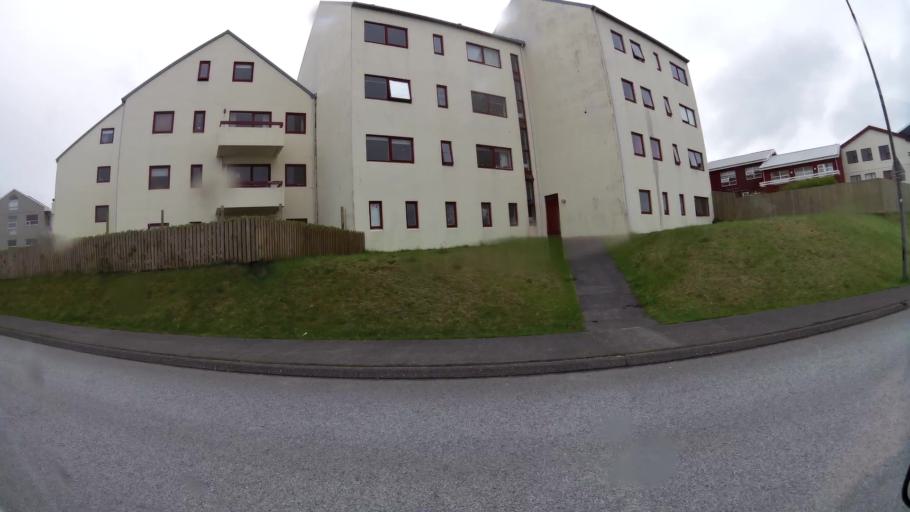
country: IS
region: Capital Region
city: Hafnarfjoerdur
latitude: 64.0569
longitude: -21.9787
